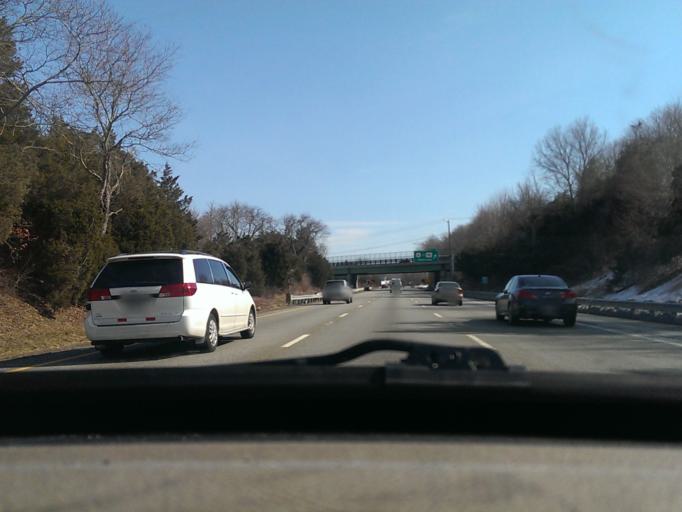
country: US
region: Massachusetts
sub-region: Bristol County
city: Ocean Grove
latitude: 41.7513
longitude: -71.2203
